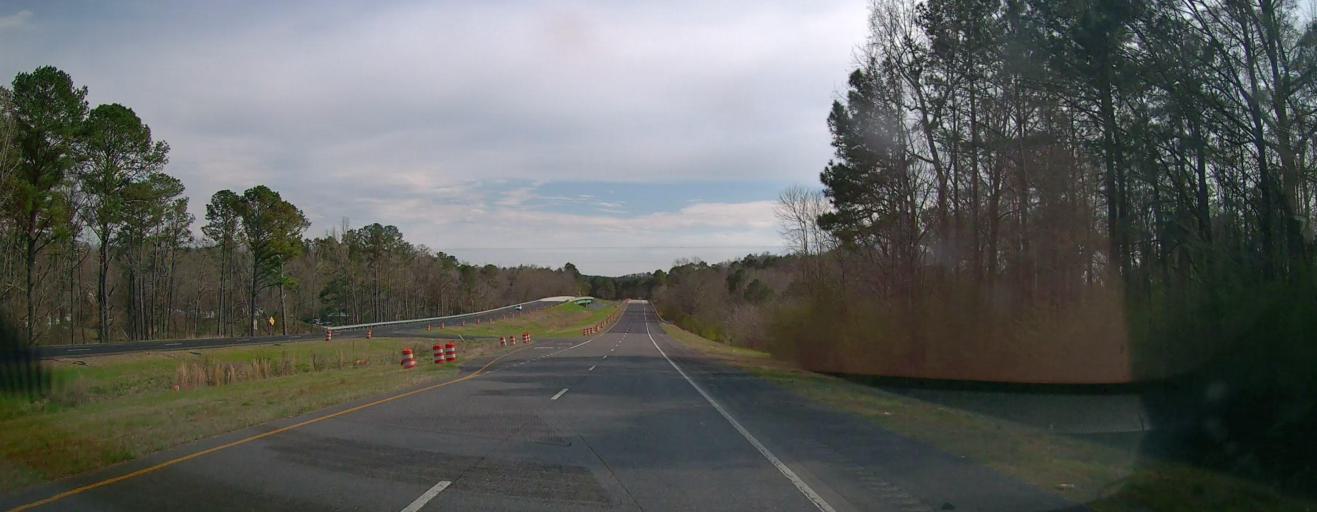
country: US
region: Alabama
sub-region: Walker County
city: Sumiton
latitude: 33.7089
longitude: -86.9931
